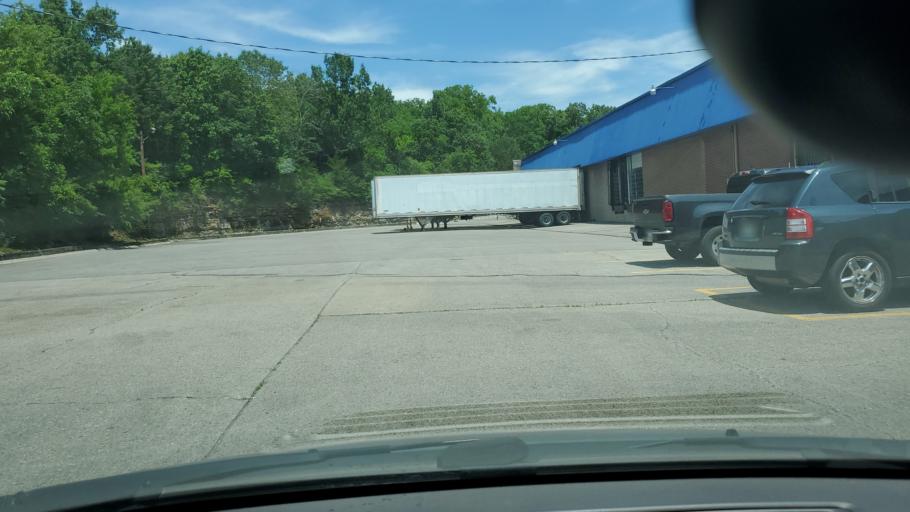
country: US
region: Tennessee
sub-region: Davidson County
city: Nashville
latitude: 36.2090
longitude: -86.7427
